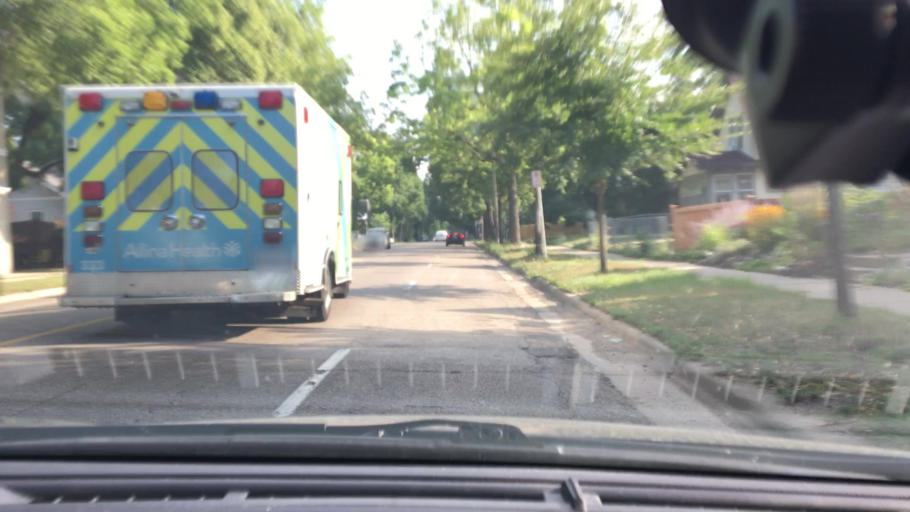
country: US
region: Minnesota
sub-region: Hennepin County
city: Minneapolis
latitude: 44.9440
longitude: -93.2475
